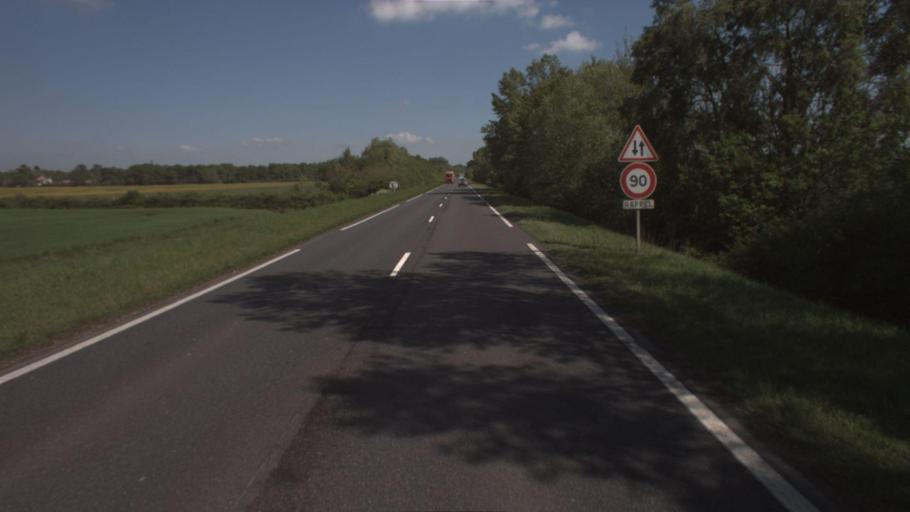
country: FR
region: Ile-de-France
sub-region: Departement de Seine-et-Marne
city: Chaumes-en-Brie
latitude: 48.6762
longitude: 2.8134
